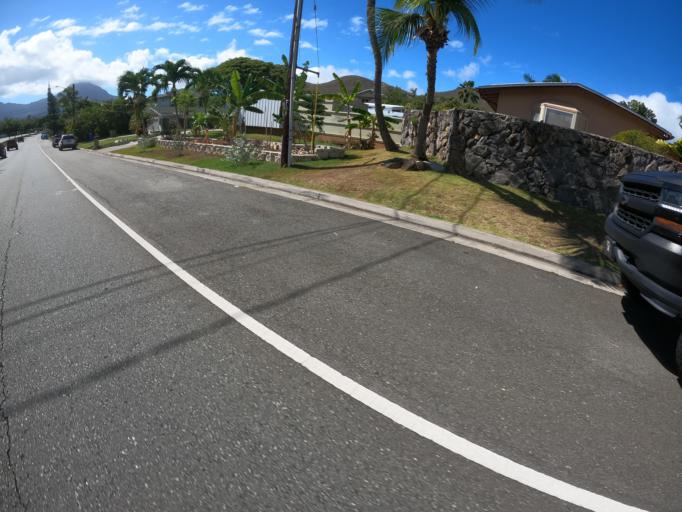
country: US
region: Hawaii
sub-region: Honolulu County
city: Kailua
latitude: 21.4150
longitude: -157.7513
